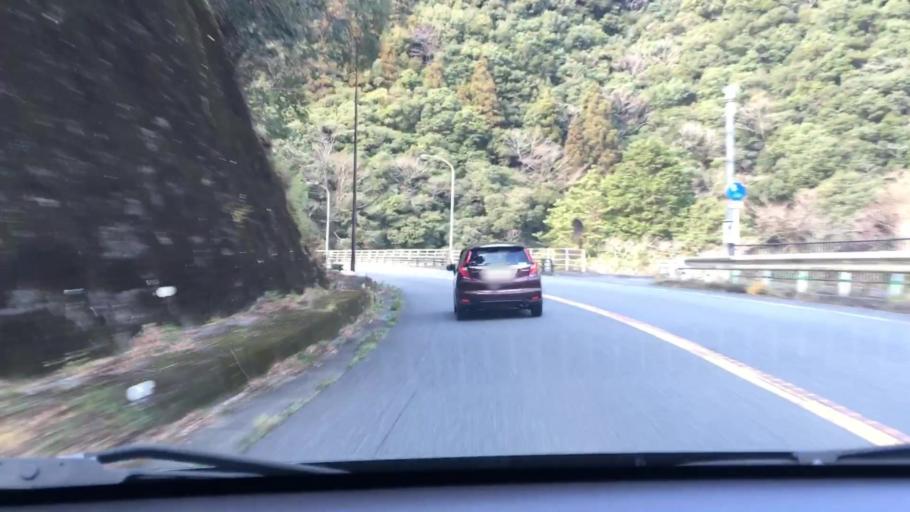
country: JP
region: Oita
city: Tsukumiura
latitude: 33.0022
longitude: 131.8035
